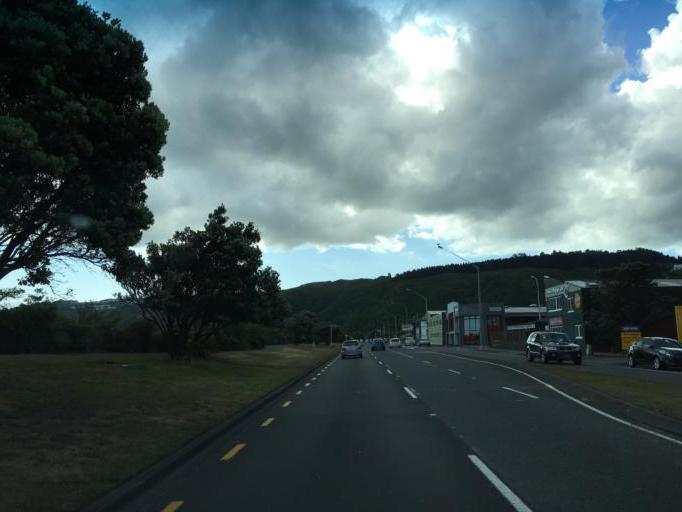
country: NZ
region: Wellington
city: Petone
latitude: -41.2262
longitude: 174.8693
